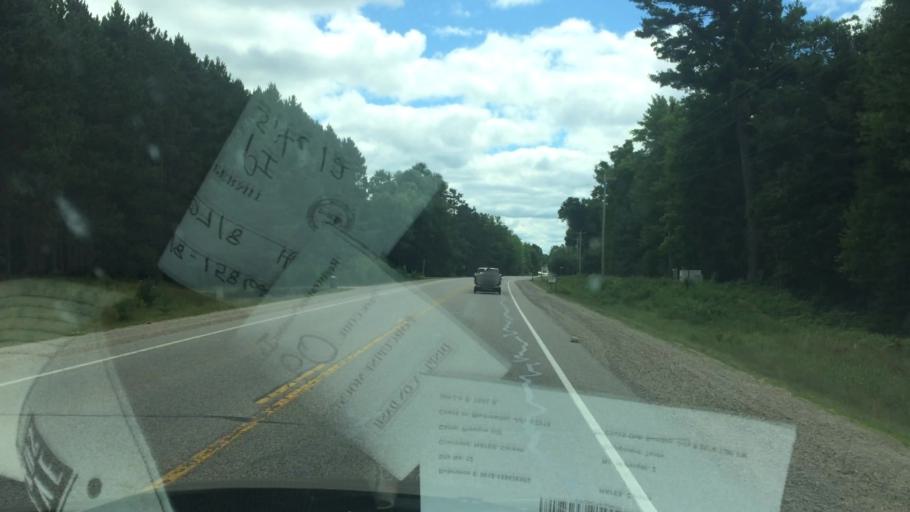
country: US
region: Wisconsin
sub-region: Vilas County
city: Eagle River
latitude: 45.8061
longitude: -89.3199
